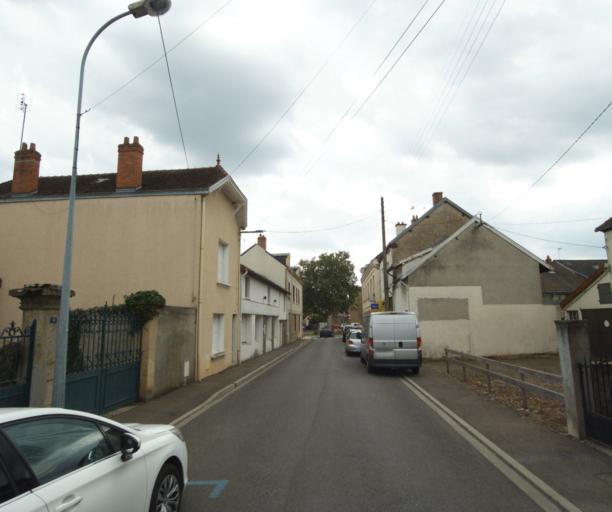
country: FR
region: Bourgogne
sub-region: Departement de Saone-et-Loire
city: Gueugnon
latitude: 46.6009
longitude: 4.0600
